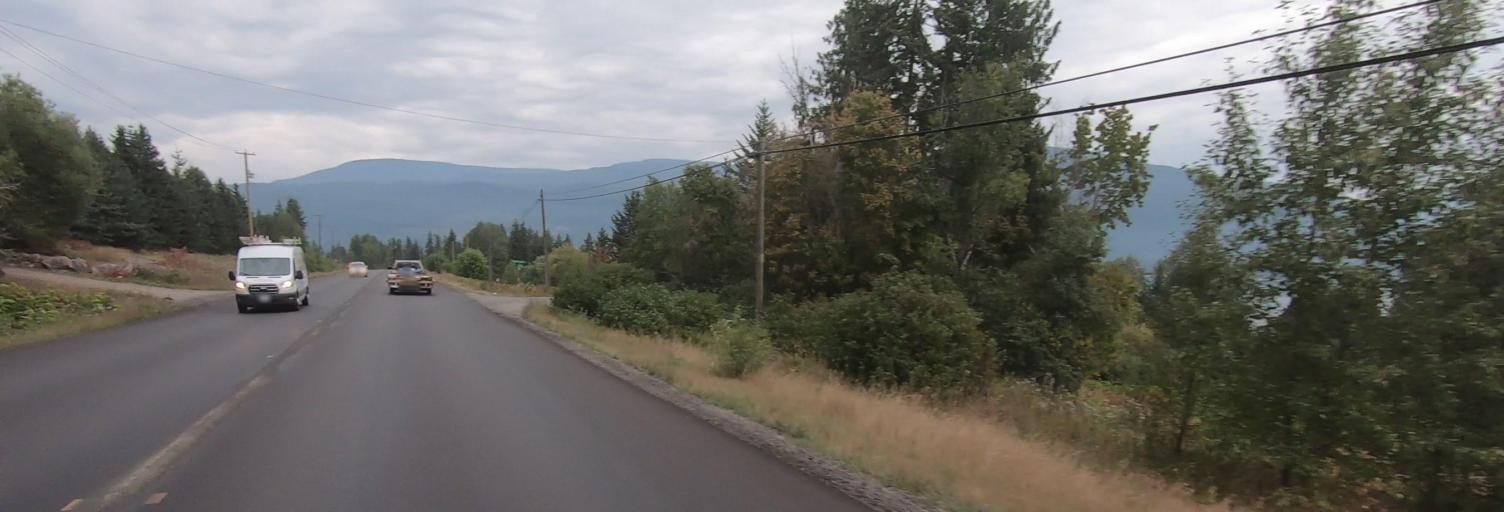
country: CA
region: British Columbia
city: Chase
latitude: 50.8869
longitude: -119.5075
